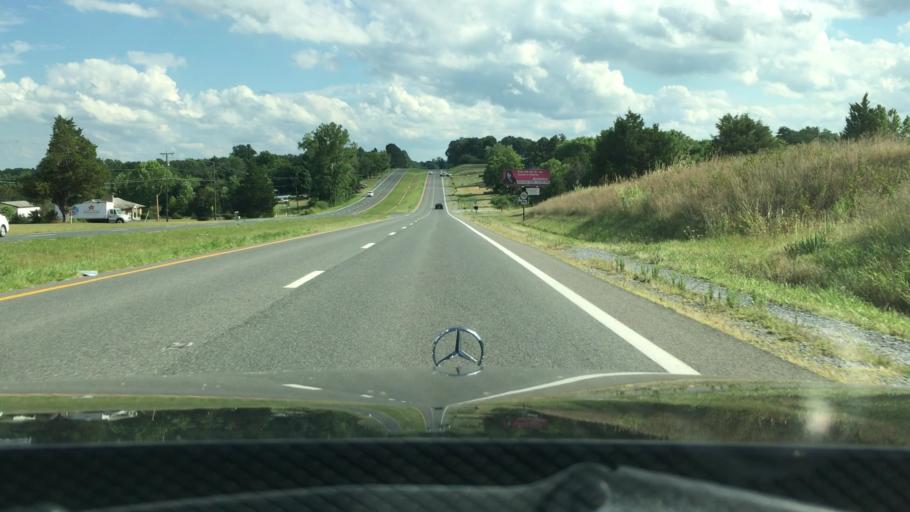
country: US
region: Virginia
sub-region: Campbell County
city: Altavista
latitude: 37.1834
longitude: -79.2045
